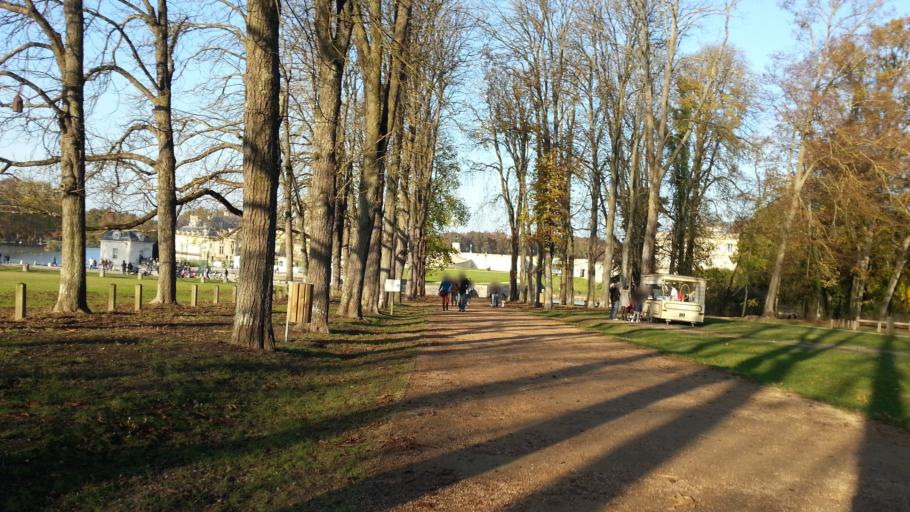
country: FR
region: Picardie
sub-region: Departement de l'Oise
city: Vineuil-Saint-Firmin
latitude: 49.1905
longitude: 2.4858
